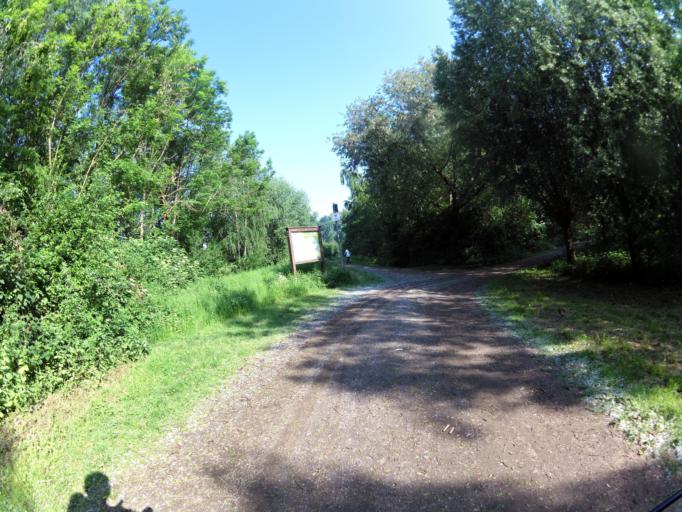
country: DE
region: North Rhine-Westphalia
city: Julich
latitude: 50.9471
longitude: 6.3236
